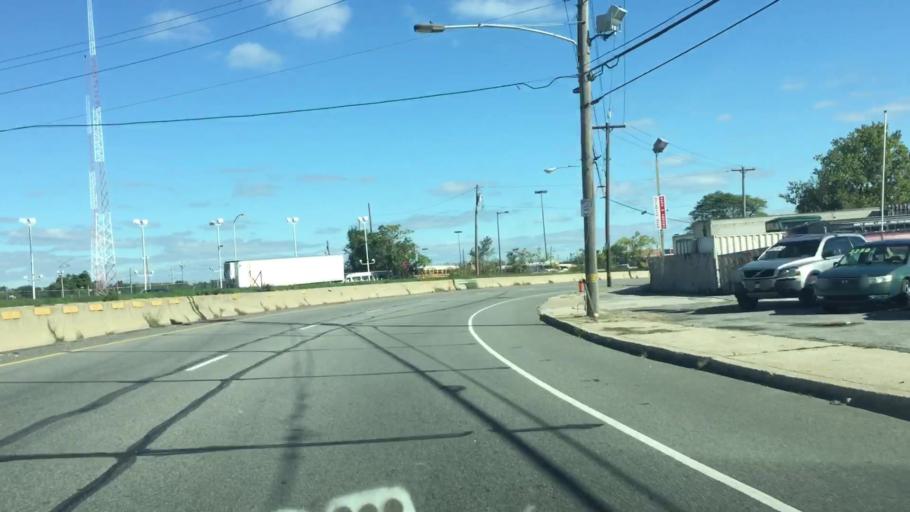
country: US
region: Pennsylvania
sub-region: Delaware County
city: Colwyn
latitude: 39.9153
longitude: -75.2211
